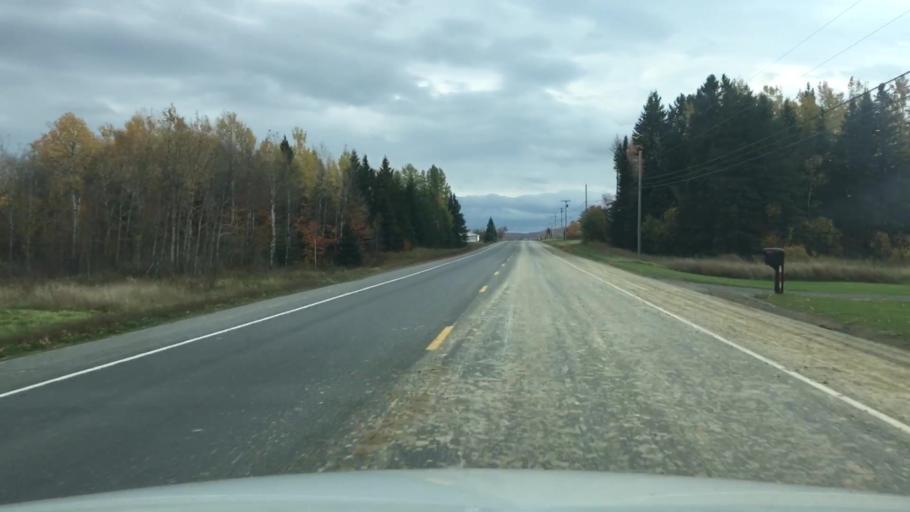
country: US
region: Maine
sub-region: Aroostook County
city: Easton
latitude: 46.5608
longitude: -67.9439
